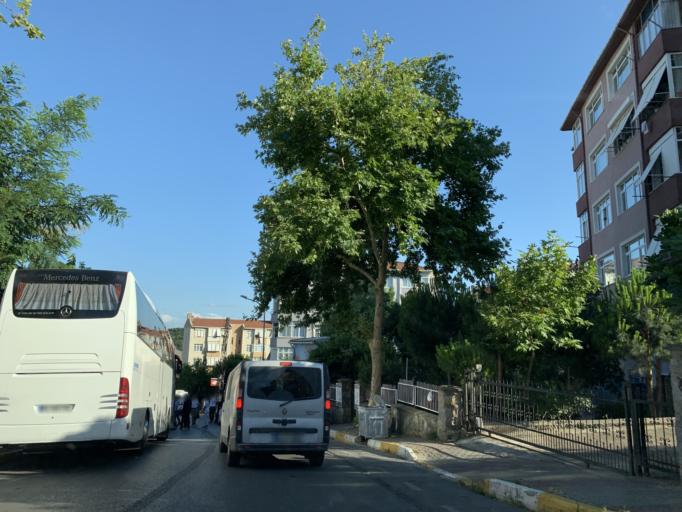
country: TR
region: Istanbul
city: Pendik
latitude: 40.8989
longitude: 29.2489
